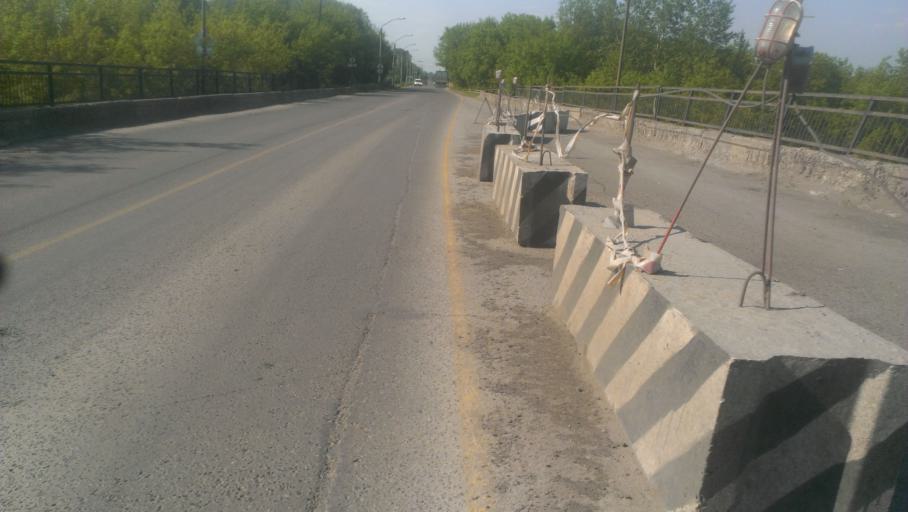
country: RU
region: Altai Krai
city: Novoaltaysk
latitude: 53.4043
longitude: 83.9453
